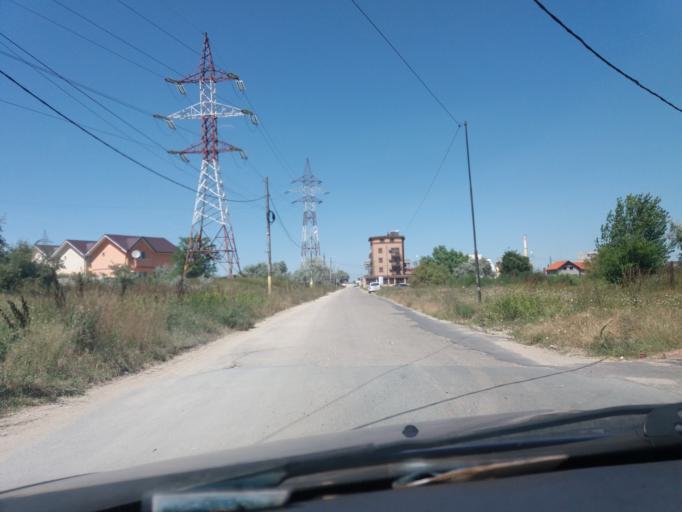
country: RO
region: Constanta
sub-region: Comuna Navodari
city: Navodari
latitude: 44.3203
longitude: 28.6283
